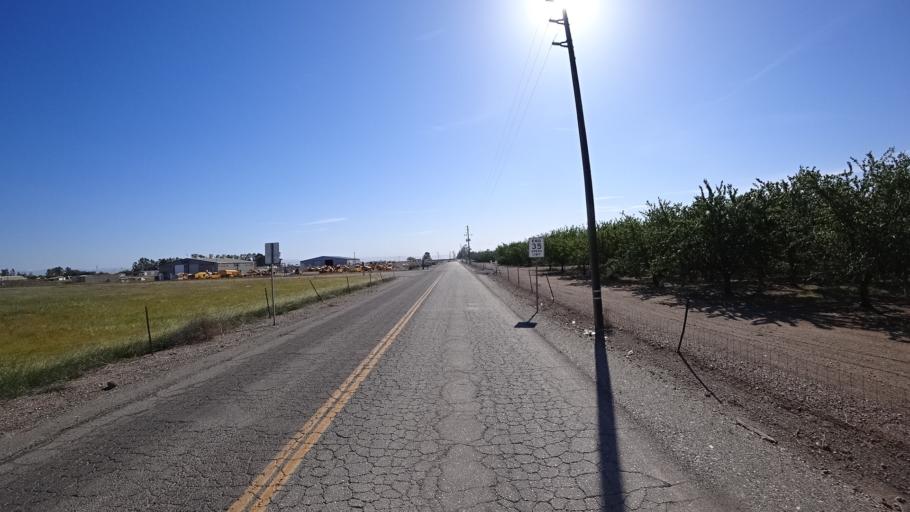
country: US
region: California
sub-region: Glenn County
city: Orland
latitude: 39.6825
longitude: -122.2010
